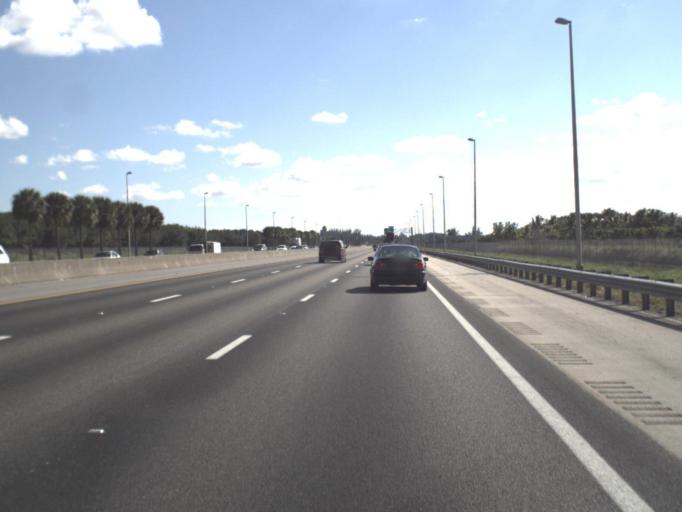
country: US
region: Florida
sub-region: Palm Beach County
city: Villages of Oriole
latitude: 26.4954
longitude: -80.1727
